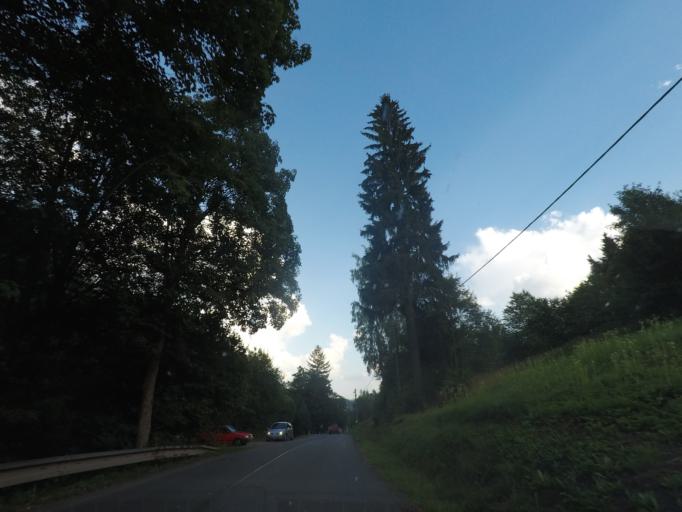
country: CZ
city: Radvanice
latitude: 50.6222
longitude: 16.1015
